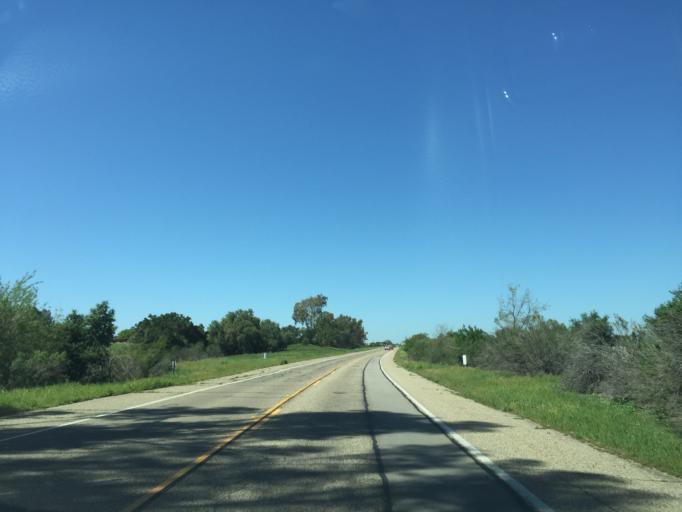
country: US
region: California
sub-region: Santa Barbara County
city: Santa Ynez
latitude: 34.6288
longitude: -120.0767
